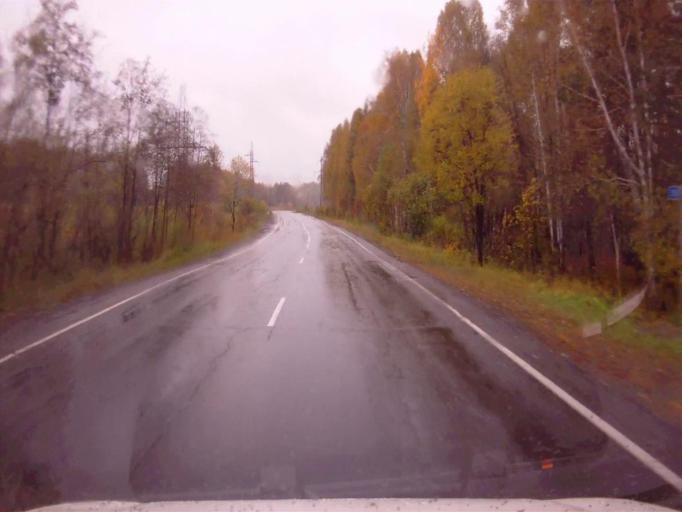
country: RU
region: Chelyabinsk
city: Verkhniy Ufaley
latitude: 55.9434
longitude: 60.4077
